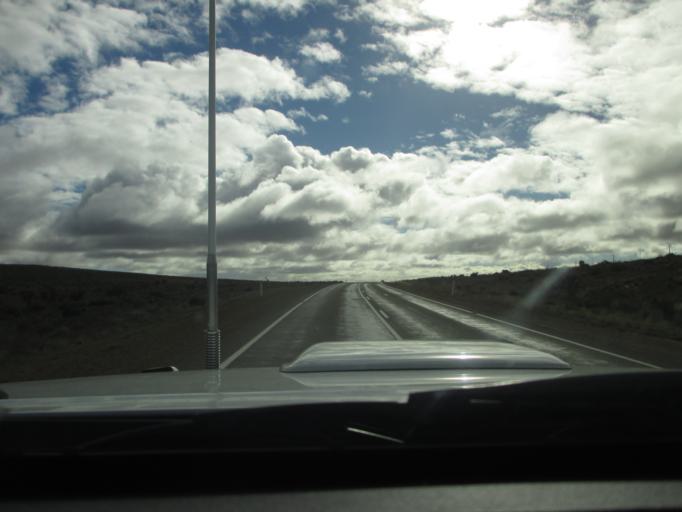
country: AU
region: South Australia
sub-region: Flinders Ranges
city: Quorn
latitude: -32.1869
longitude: 138.5361
